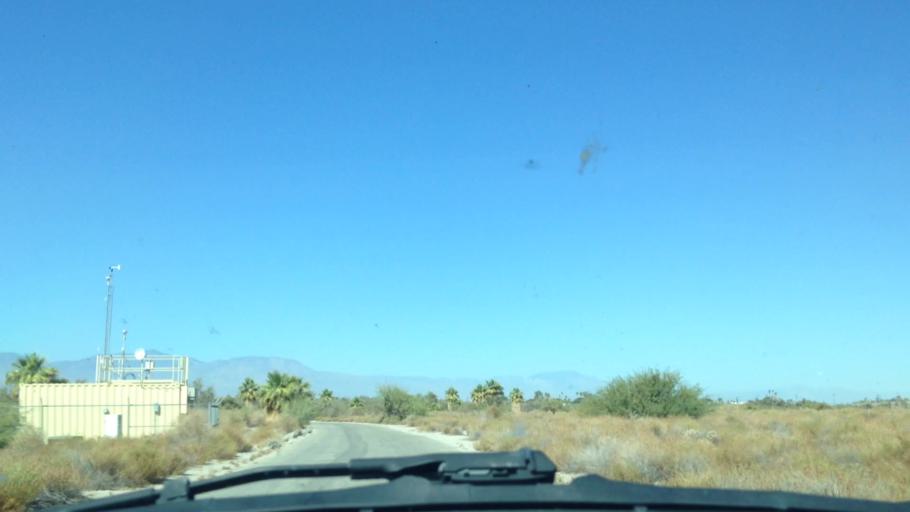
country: US
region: California
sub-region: Imperial County
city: Desert Shores
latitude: 33.5090
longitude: -115.9191
